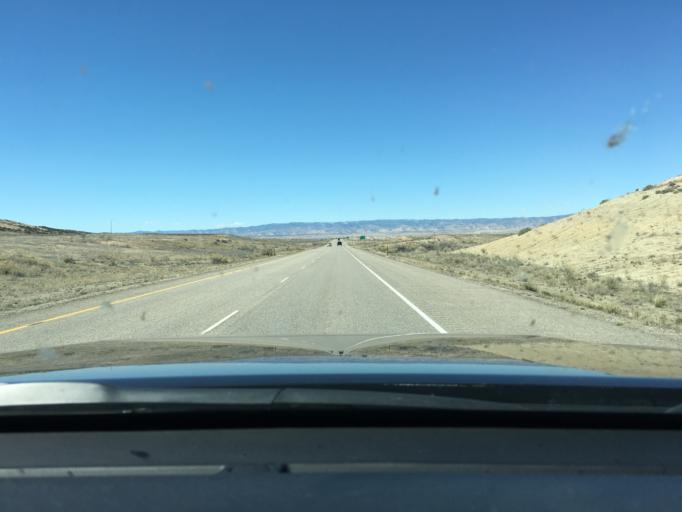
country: US
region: Colorado
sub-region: Mesa County
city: Loma
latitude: 39.2093
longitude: -108.8614
